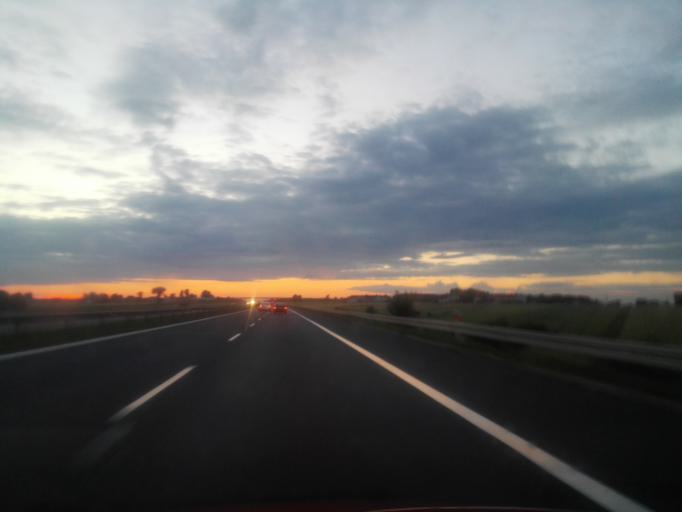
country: PL
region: Lodz Voivodeship
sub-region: Powiat piotrkowski
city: Moszczenica
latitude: 51.4709
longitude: 19.6317
